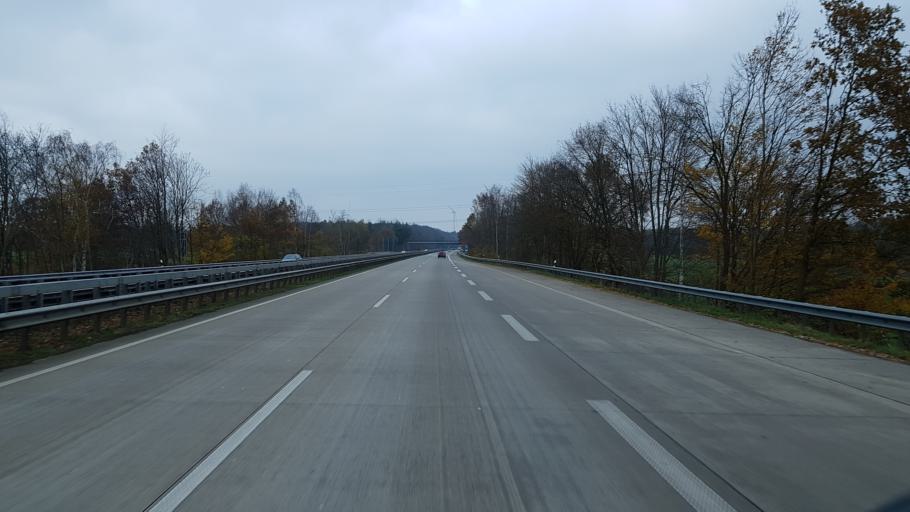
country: DE
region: Lower Saxony
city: Schwanewede
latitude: 53.2311
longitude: 8.6411
